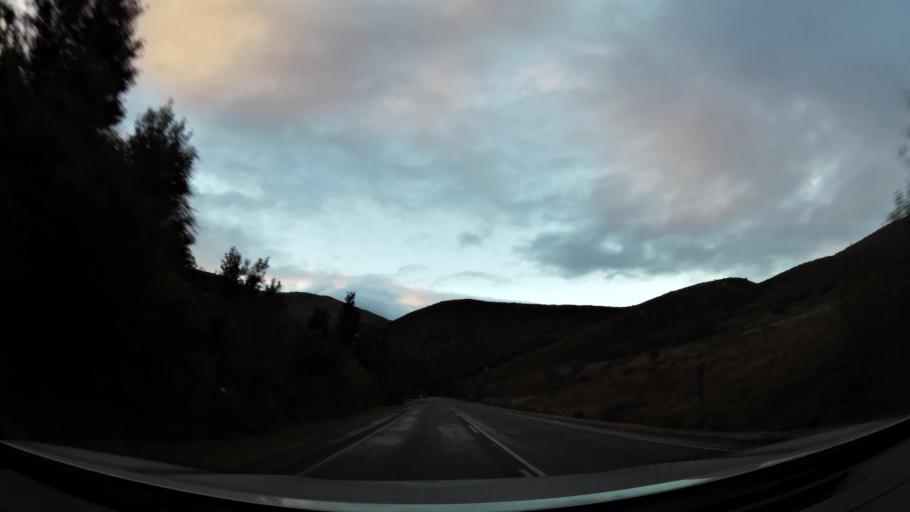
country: ZA
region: Western Cape
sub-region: Overberg District Municipality
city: Swellendam
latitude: -33.9882
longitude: 20.7175
